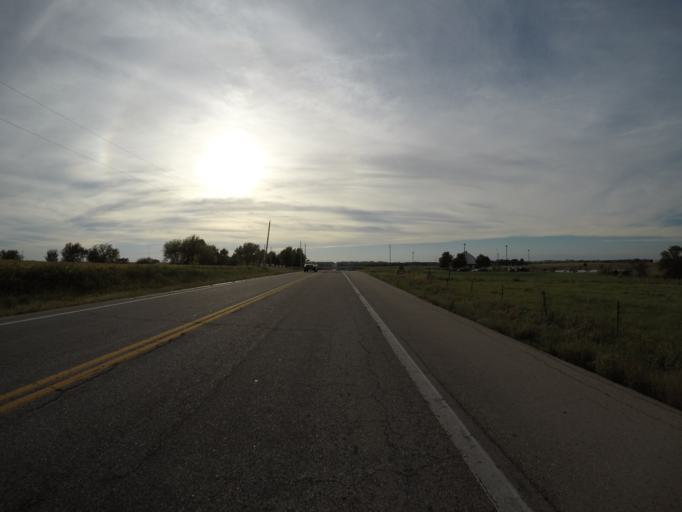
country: US
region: Kansas
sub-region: Douglas County
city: Baldwin City
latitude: 38.7824
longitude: -95.2637
